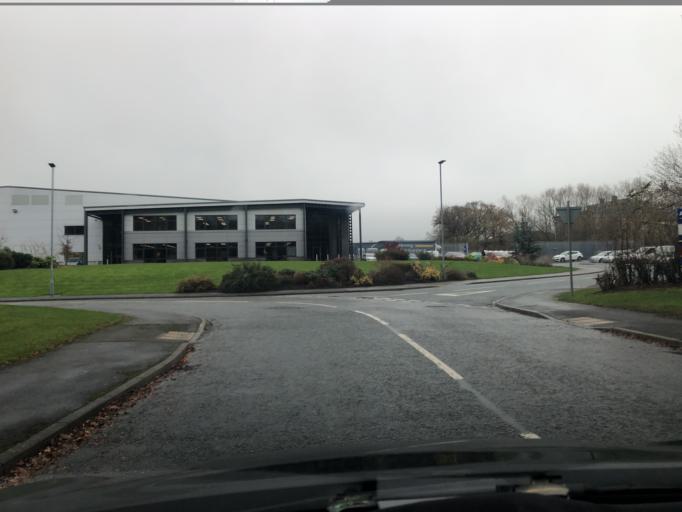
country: GB
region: England
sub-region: North Yorkshire
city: Stokesley
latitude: 54.4641
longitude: -1.1737
